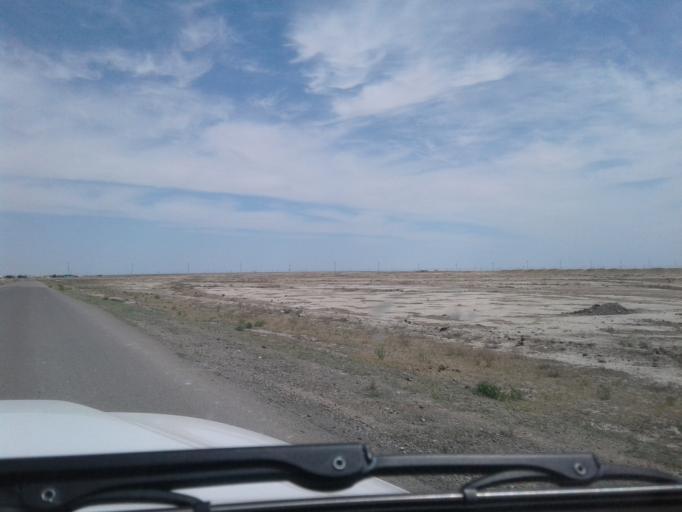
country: TM
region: Balkan
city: Gazanjyk
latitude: 39.1979
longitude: 55.7074
